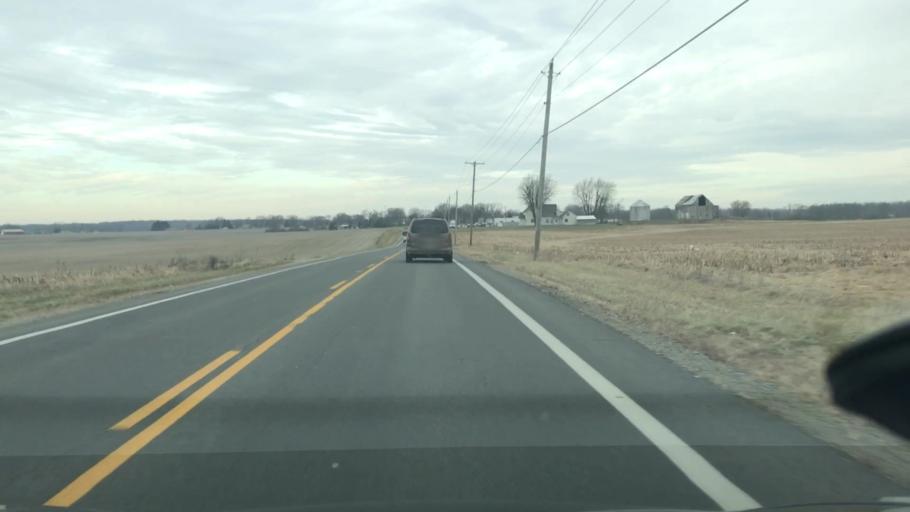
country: US
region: Ohio
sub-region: Madison County
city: Choctaw Lake
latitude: 39.9237
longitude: -83.4858
